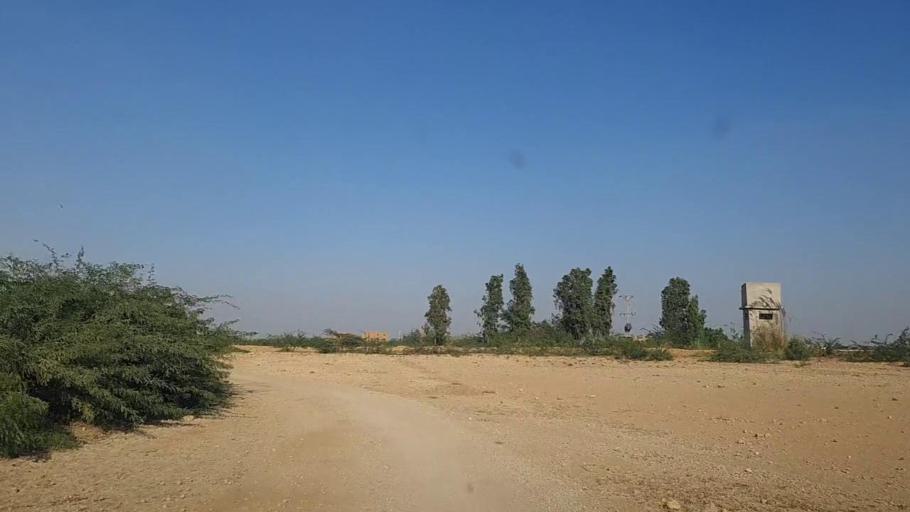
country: PK
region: Sindh
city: Daro Mehar
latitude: 25.0488
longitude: 68.1373
